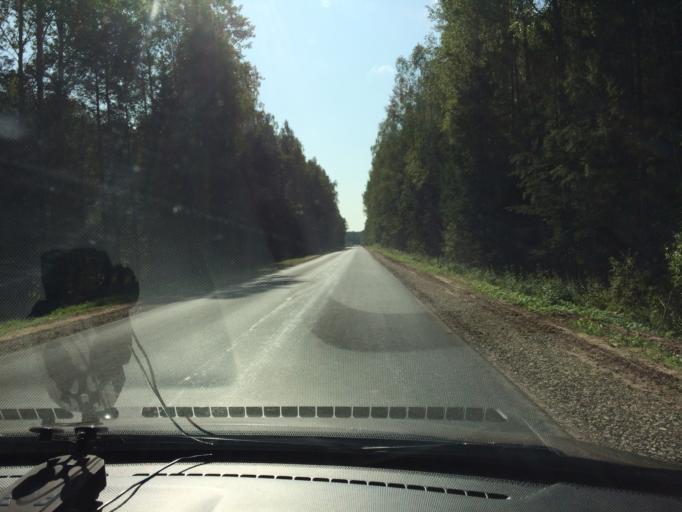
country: RU
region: Mariy-El
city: Surok
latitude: 56.5589
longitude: 48.3079
